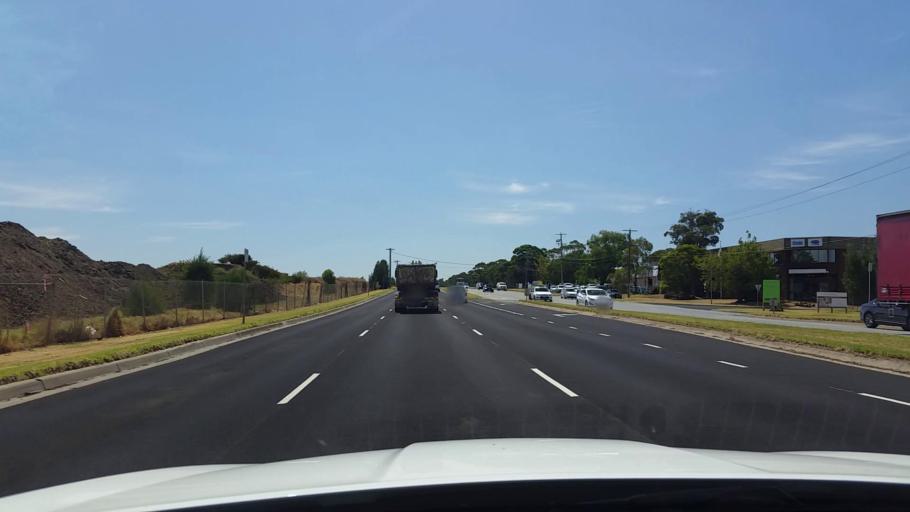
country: AU
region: Victoria
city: Heatherton
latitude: -37.9844
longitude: 145.1096
